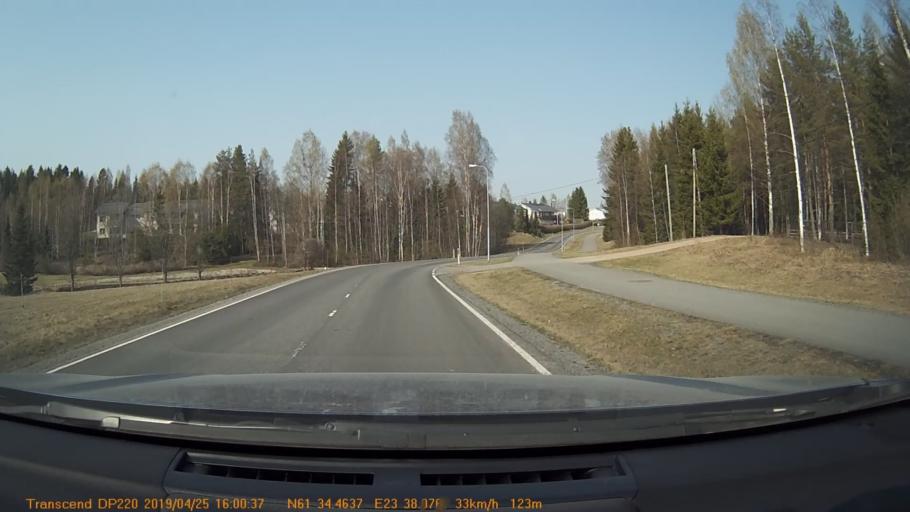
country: FI
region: Pirkanmaa
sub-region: Tampere
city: Yloejaervi
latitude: 61.5744
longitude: 23.6347
